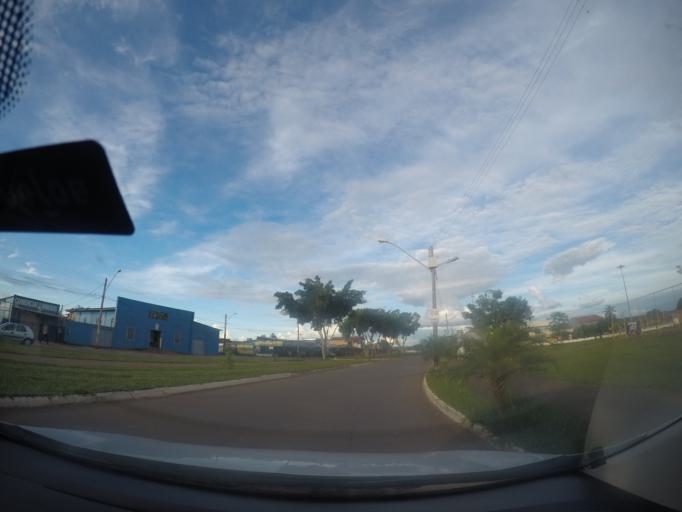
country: BR
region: Goias
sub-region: Goianira
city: Goianira
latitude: -16.5901
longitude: -49.3783
